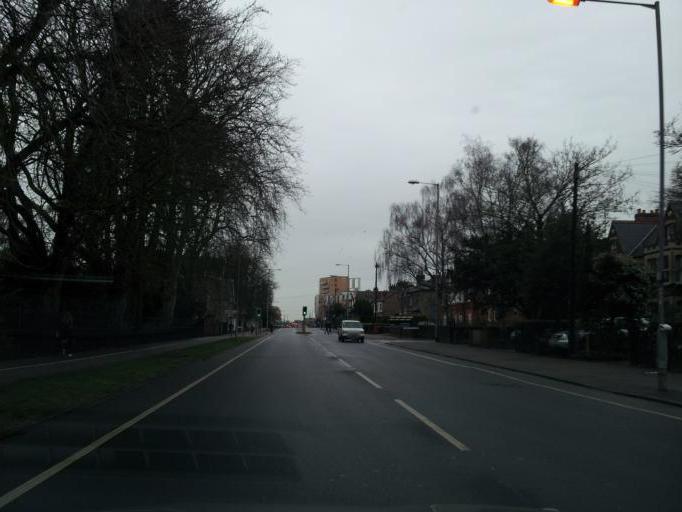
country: GB
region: England
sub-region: Cambridgeshire
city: Cambridge
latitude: 52.1859
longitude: 0.1380
